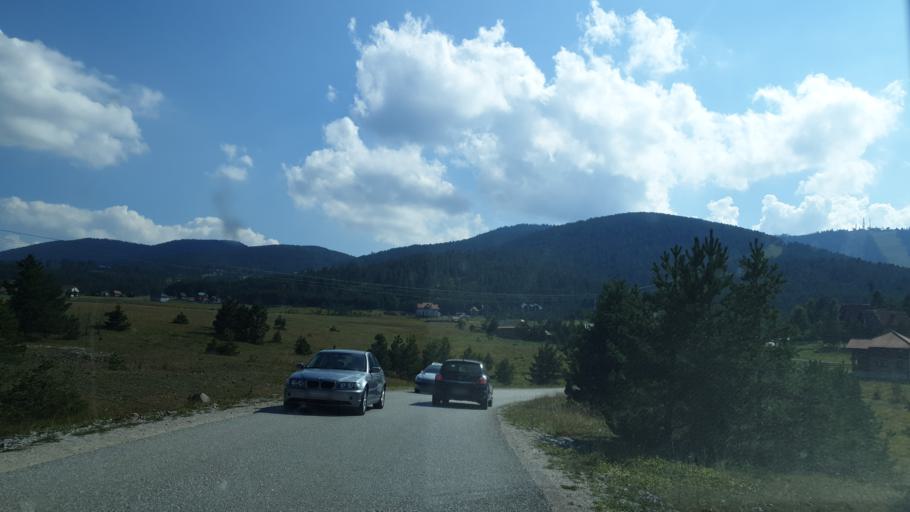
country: RS
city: Zlatibor
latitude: 43.6770
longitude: 19.6554
